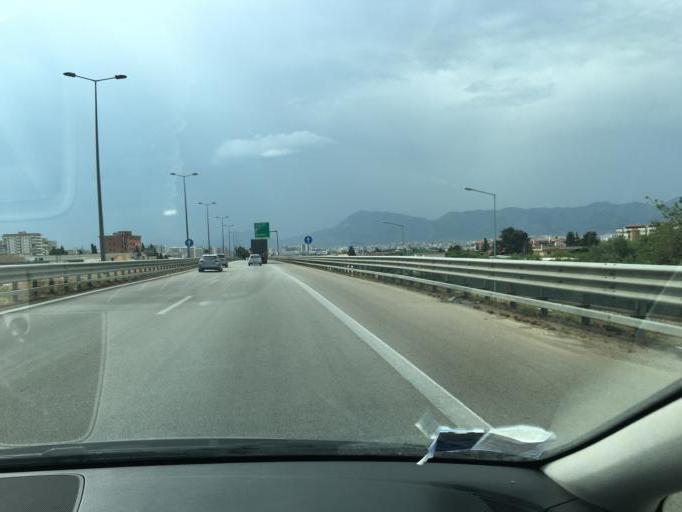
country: IT
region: Sicily
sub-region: Palermo
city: Palermo
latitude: 38.1575
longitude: 13.3155
